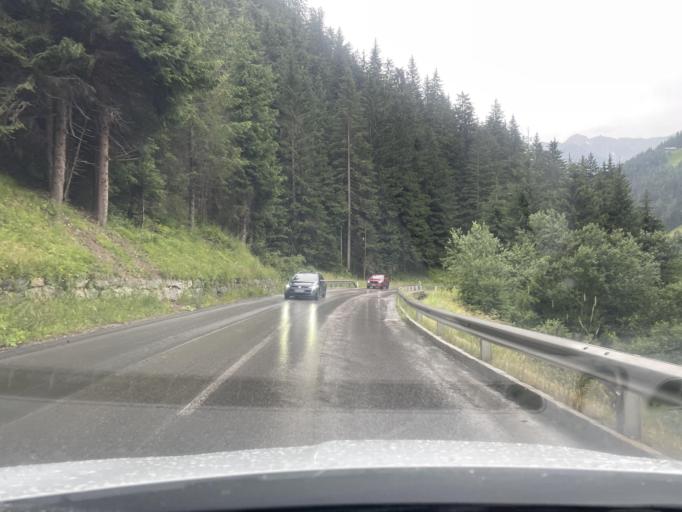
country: AT
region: Tyrol
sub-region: Politischer Bezirk Lienz
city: Ausservillgraten
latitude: 46.7724
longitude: 12.4290
